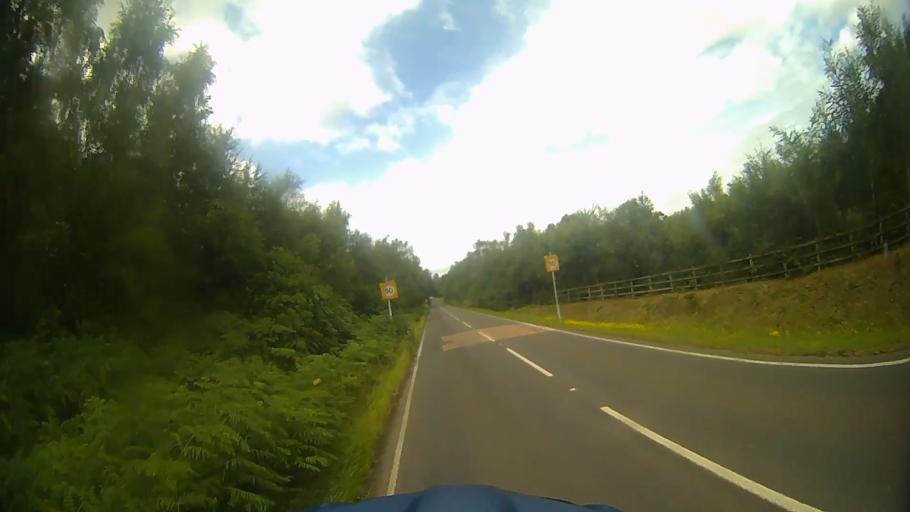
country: GB
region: England
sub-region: Wokingham
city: Barkham
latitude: 51.4069
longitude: -0.8749
